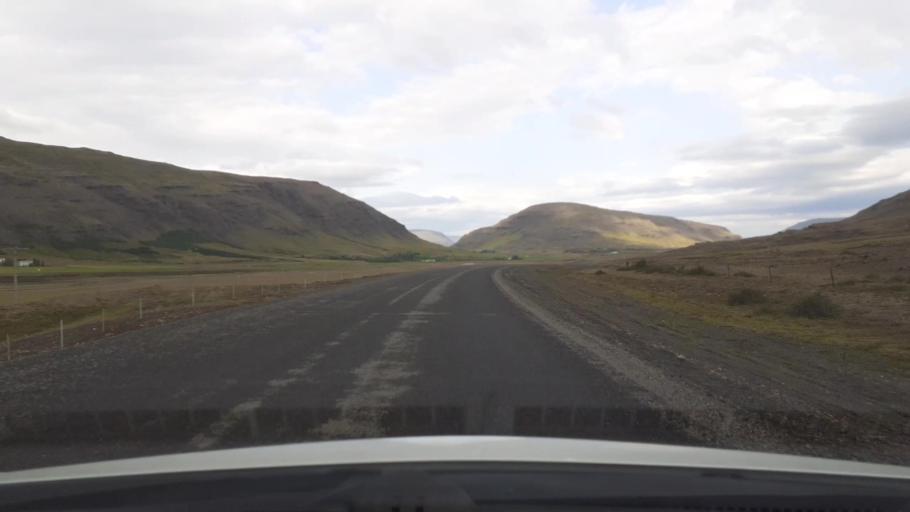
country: IS
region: Capital Region
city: Mosfellsbaer
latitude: 64.2967
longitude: -21.4645
